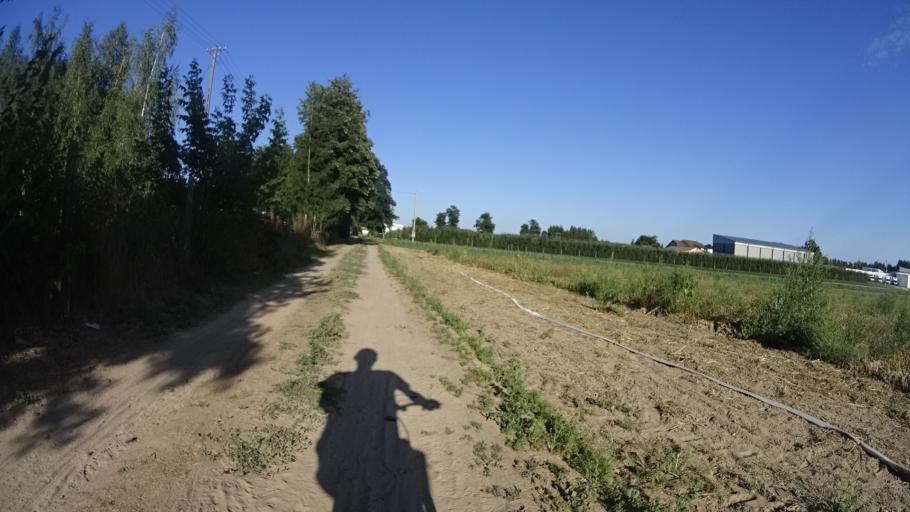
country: PL
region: Masovian Voivodeship
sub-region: Powiat bialobrzeski
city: Wysmierzyce
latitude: 51.6740
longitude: 20.8274
